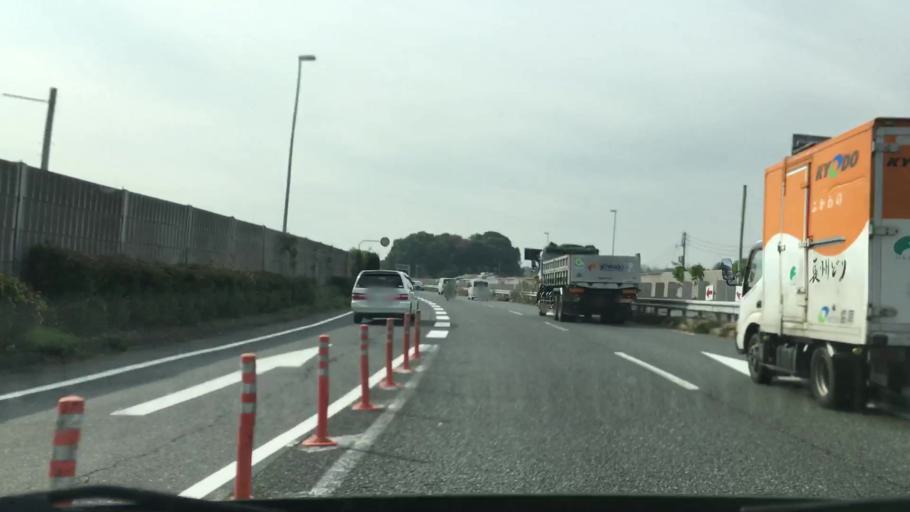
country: JP
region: Hiroshima
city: Hatsukaichi
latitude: 34.3811
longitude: 132.3504
